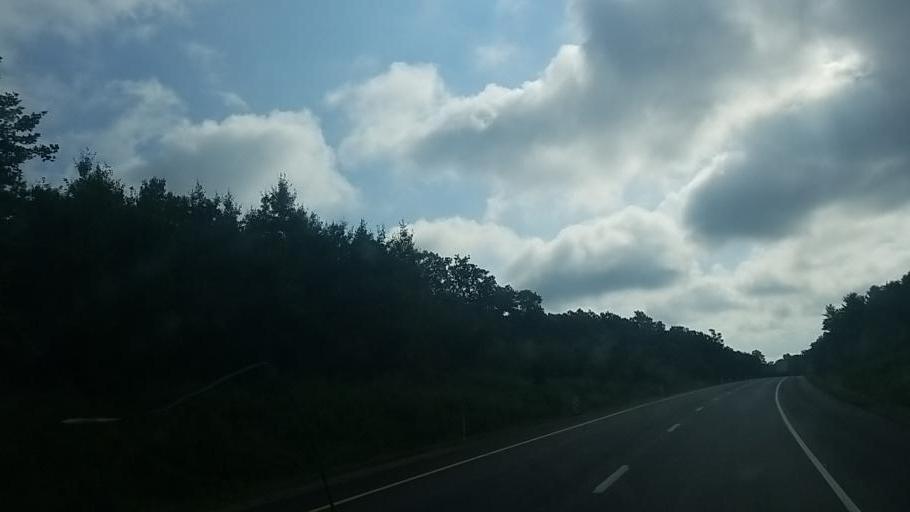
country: US
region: Pennsylvania
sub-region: Clearfield County
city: Troy
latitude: 40.9751
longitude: -78.0541
